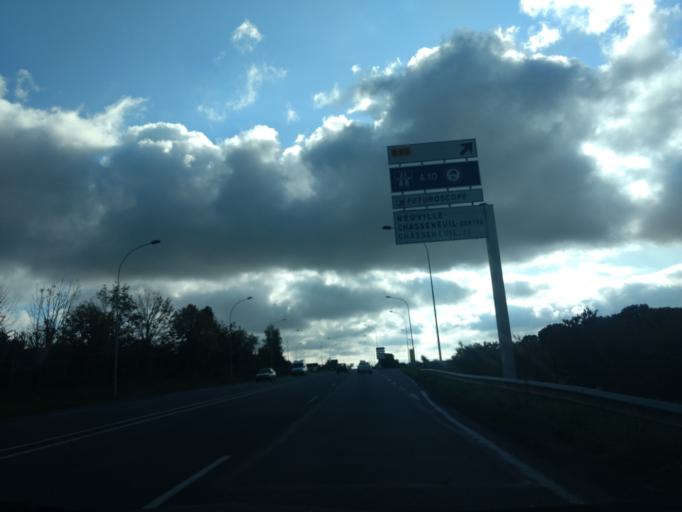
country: FR
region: Poitou-Charentes
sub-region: Departement de la Vienne
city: Chasseneuil-du-Poitou
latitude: 46.6630
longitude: 0.3704
